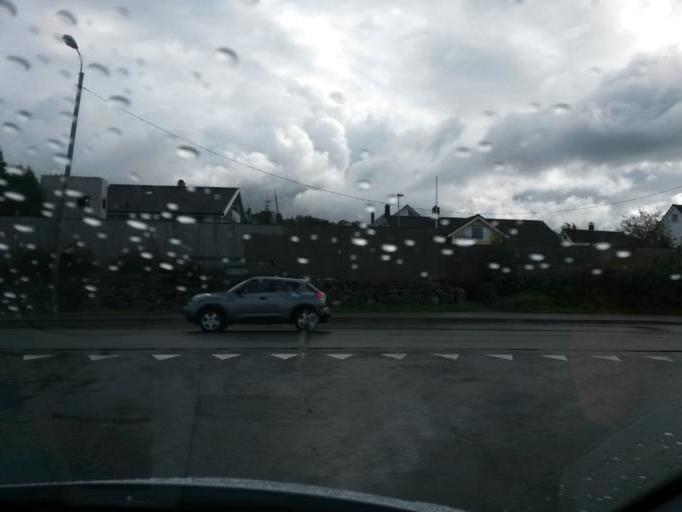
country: NO
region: Rogaland
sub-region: Sandnes
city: Sandnes
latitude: 58.8882
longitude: 5.7291
